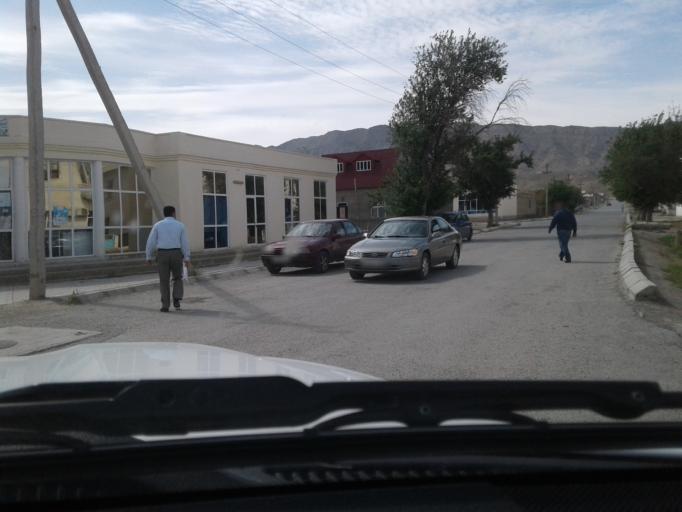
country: TM
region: Balkan
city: Gazanjyk
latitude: 39.2446
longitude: 55.5090
